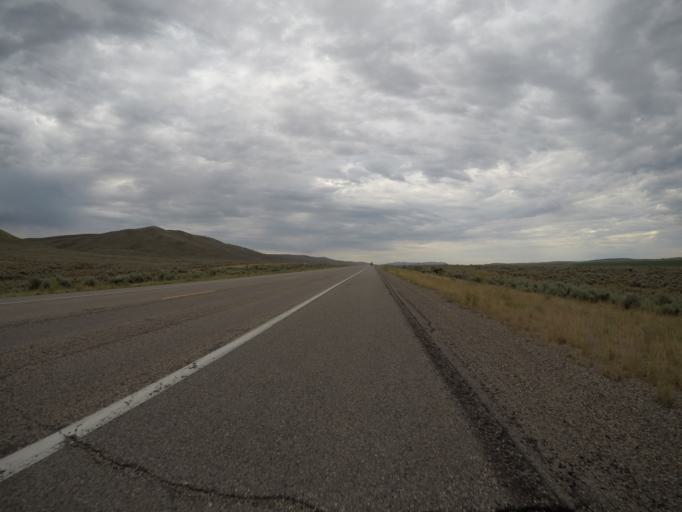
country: US
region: Utah
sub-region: Rich County
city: Randolph
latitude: 41.8637
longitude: -110.9700
